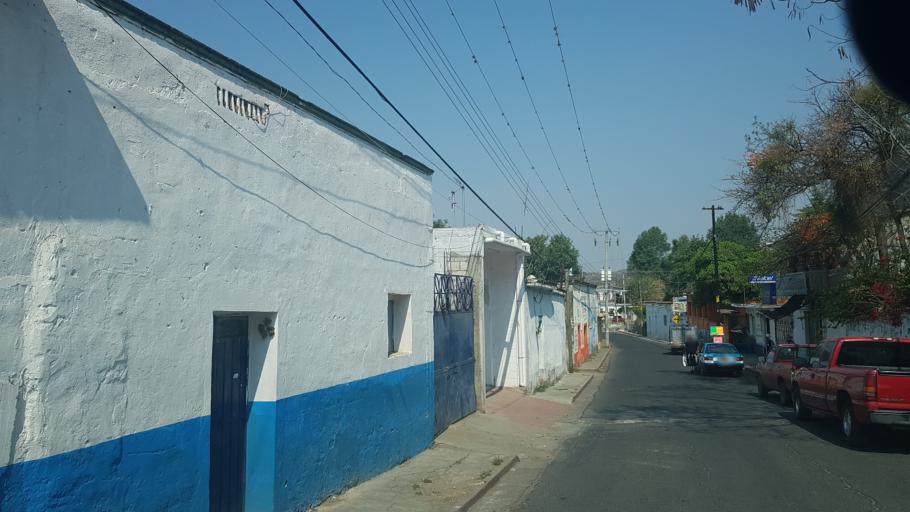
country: MX
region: Morelos
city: Tlacotepec
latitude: 18.8144
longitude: -98.7514
